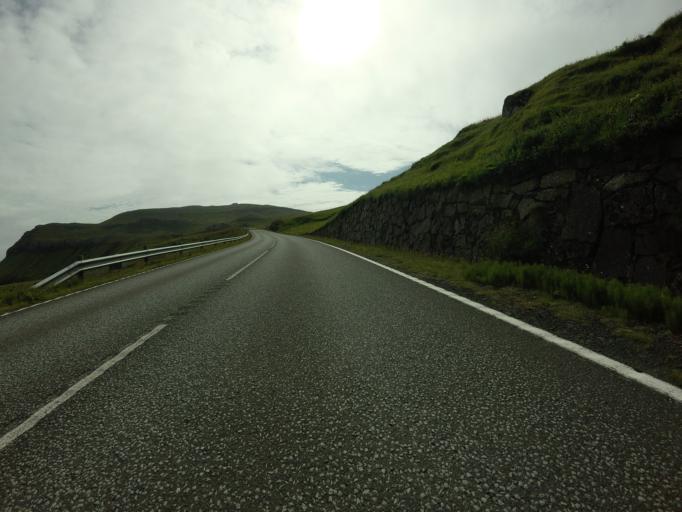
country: FO
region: Sandoy
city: Sandur
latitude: 61.8974
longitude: -6.8715
